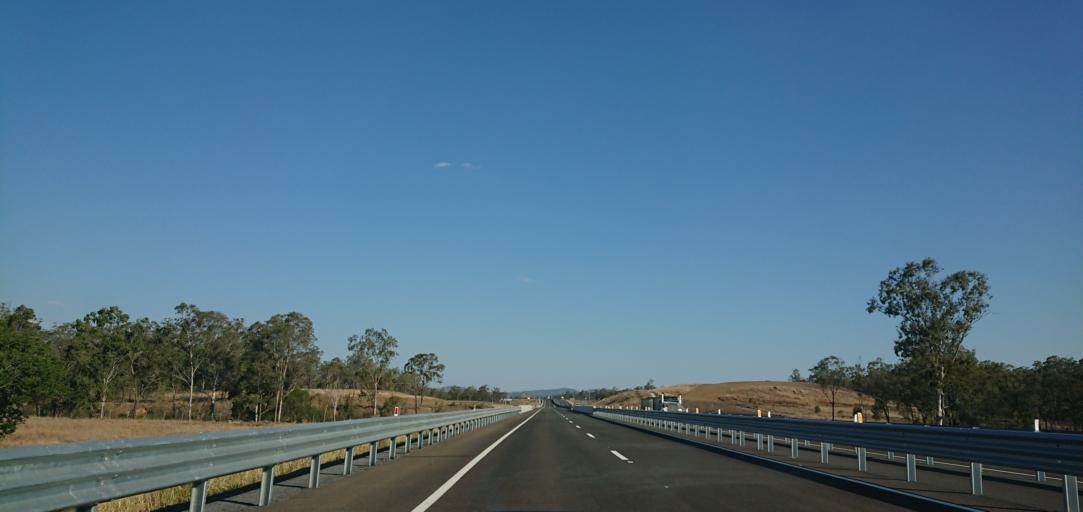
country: AU
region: Queensland
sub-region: Toowoomba
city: Rangeville
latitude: -27.5351
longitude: 152.0758
